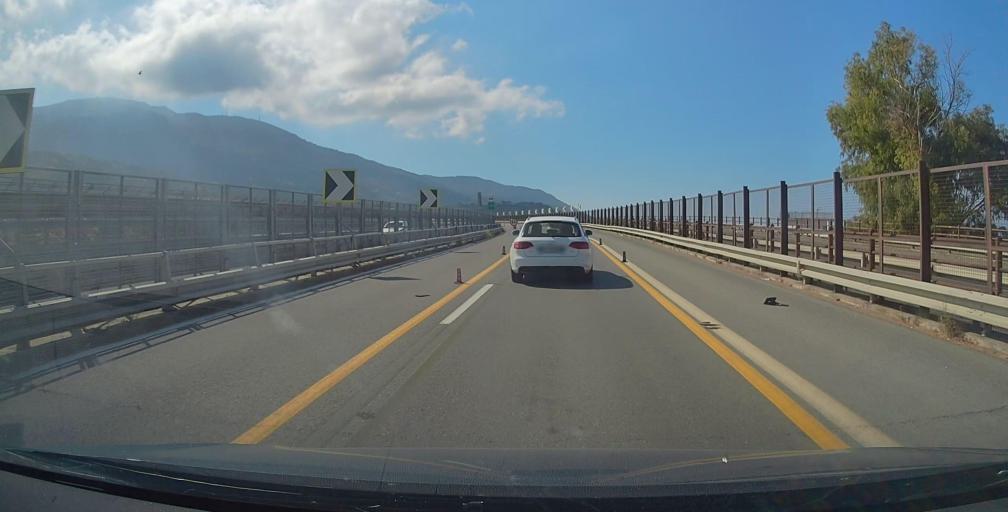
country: IT
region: Sicily
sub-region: Messina
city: Patti
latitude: 38.1482
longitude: 14.9752
